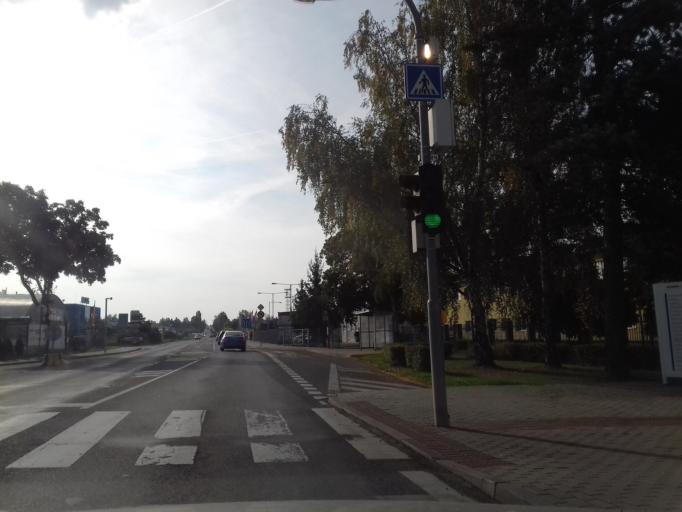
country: CZ
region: Central Bohemia
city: Vestec
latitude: 49.9858
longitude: 14.4939
